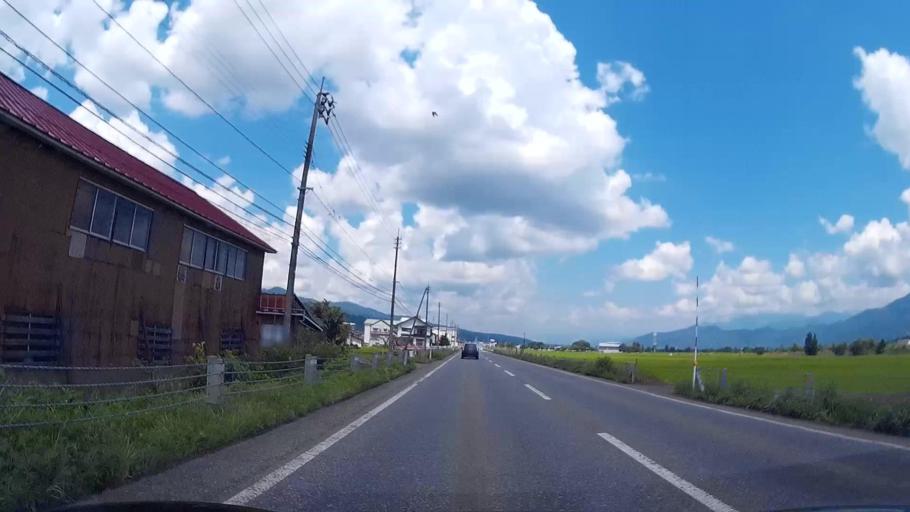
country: JP
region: Niigata
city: Shiozawa
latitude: 36.9971
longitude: 138.8136
